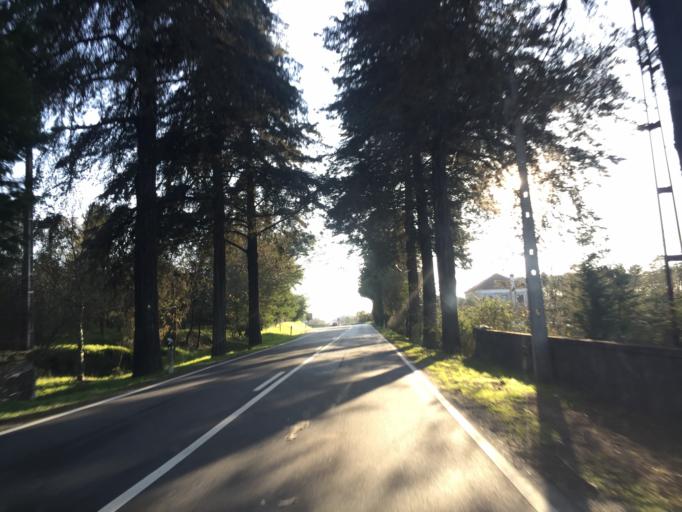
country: PT
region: Viseu
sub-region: Nelas
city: Nelas
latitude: 40.4884
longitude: -7.9072
